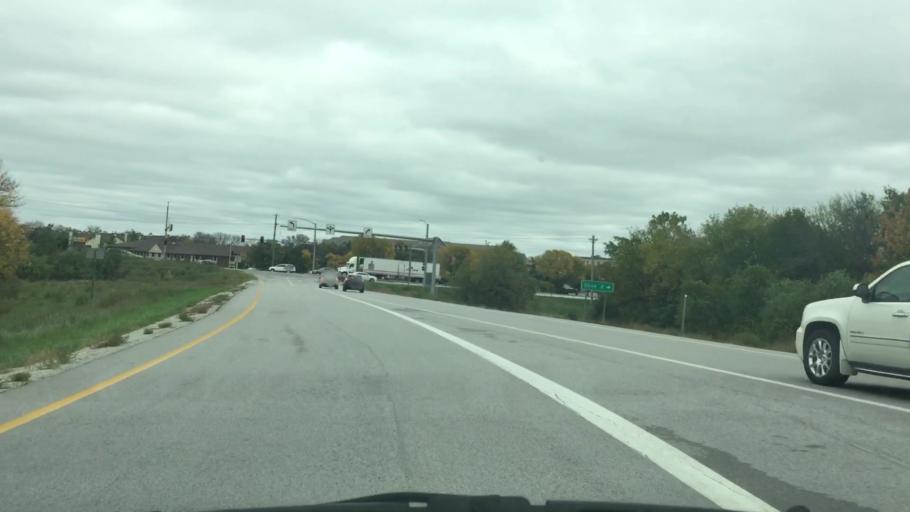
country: US
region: Iowa
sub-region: Polk County
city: Clive
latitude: 41.5991
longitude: -93.7752
